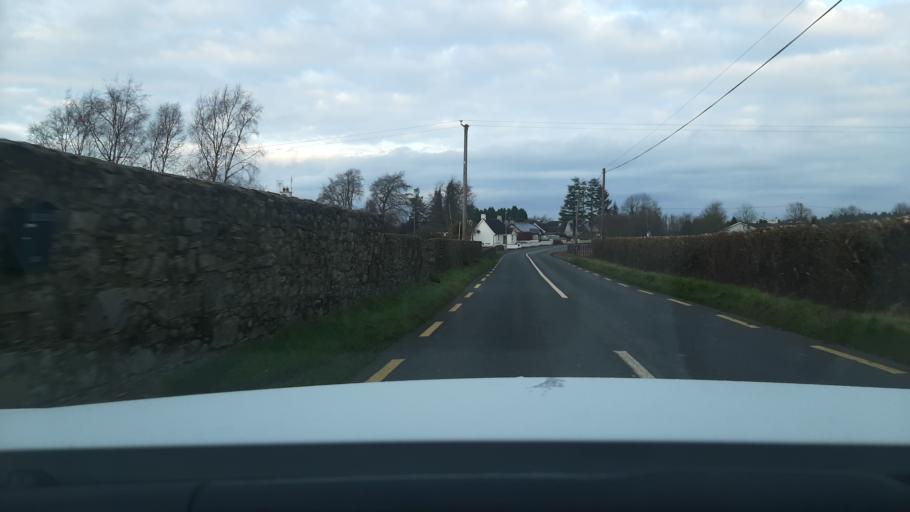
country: IE
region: Leinster
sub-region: Kildare
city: Rathangan
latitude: 53.2335
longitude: -7.0093
